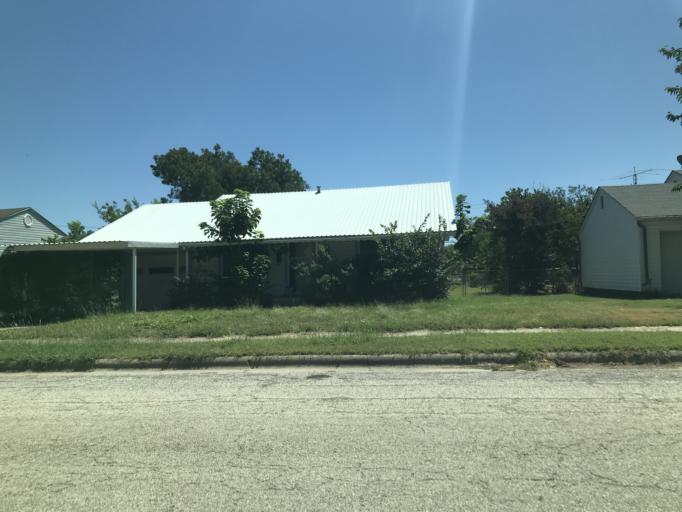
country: US
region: Texas
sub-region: Taylor County
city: Abilene
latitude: 32.4226
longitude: -99.7424
